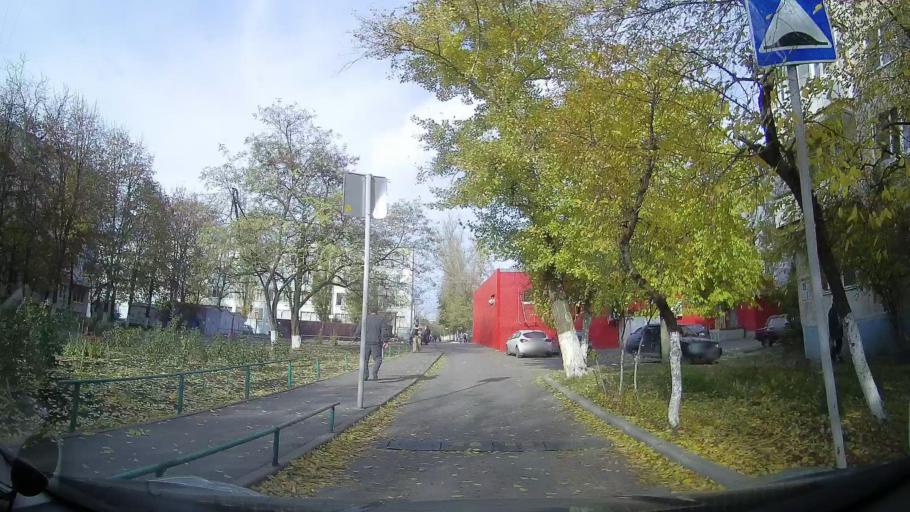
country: RU
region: Rostov
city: Severnyy
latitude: 47.2800
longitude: 39.7127
